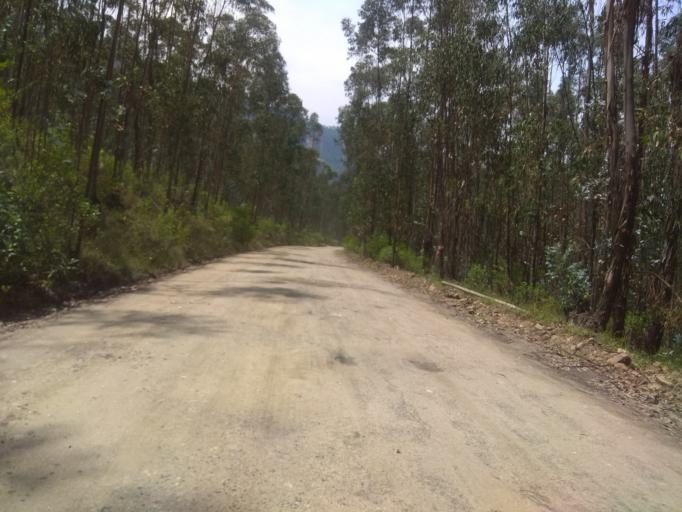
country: CO
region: Boyaca
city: Socha Viejo
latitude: 5.9788
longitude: -72.7359
